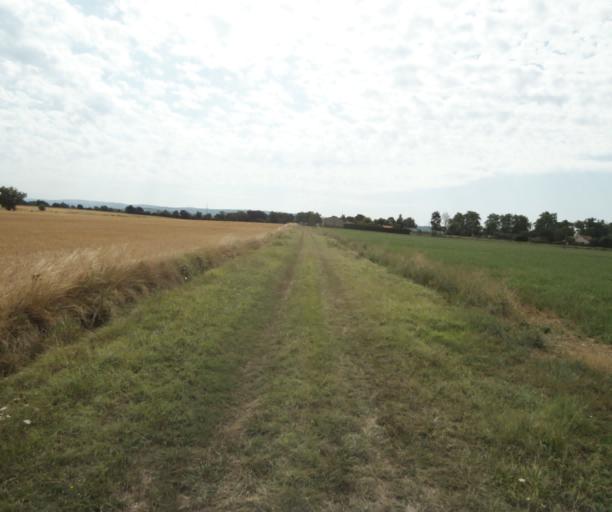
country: FR
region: Midi-Pyrenees
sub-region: Departement de la Haute-Garonne
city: Saint-Felix-Lauragais
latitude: 43.4495
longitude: 1.9277
